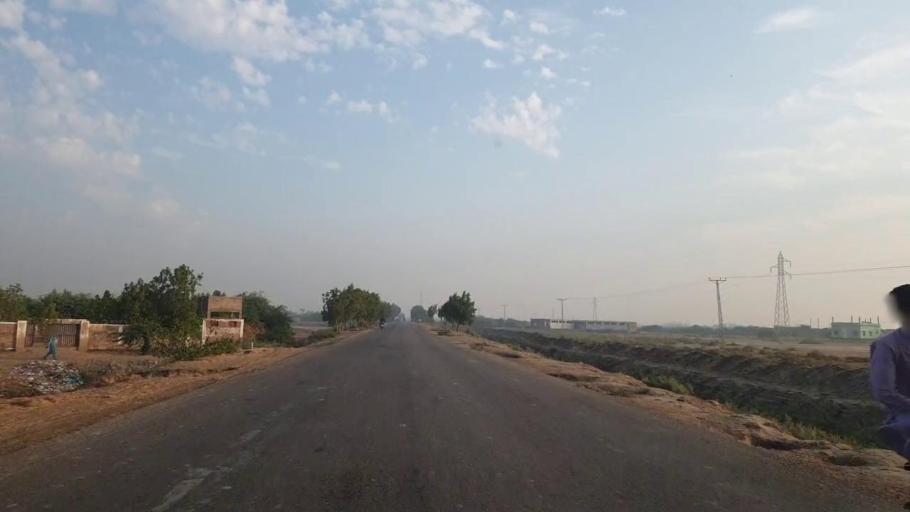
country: PK
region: Sindh
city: Badin
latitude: 24.6885
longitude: 68.9149
